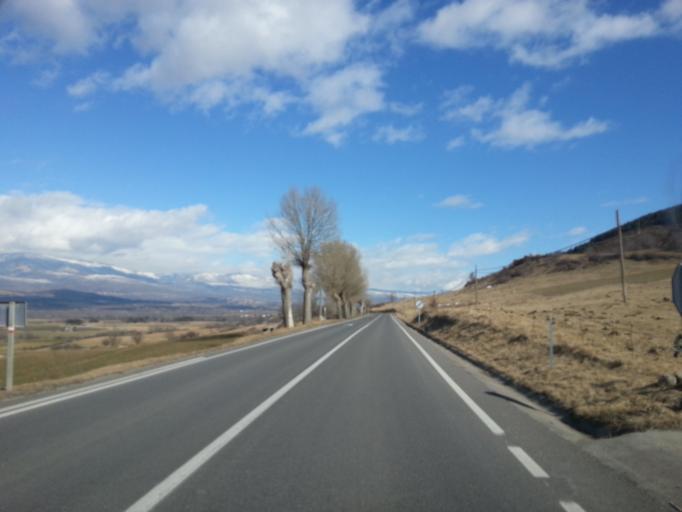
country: ES
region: Catalonia
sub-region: Provincia de Girona
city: Das
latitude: 42.3640
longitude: 1.8741
